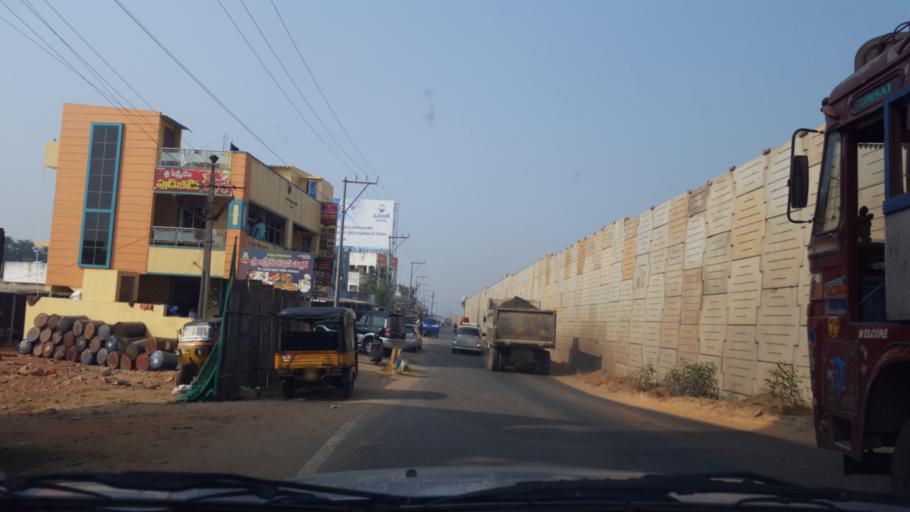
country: IN
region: Andhra Pradesh
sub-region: Srikakulam
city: Srikakulam
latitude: 18.2713
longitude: 83.8050
